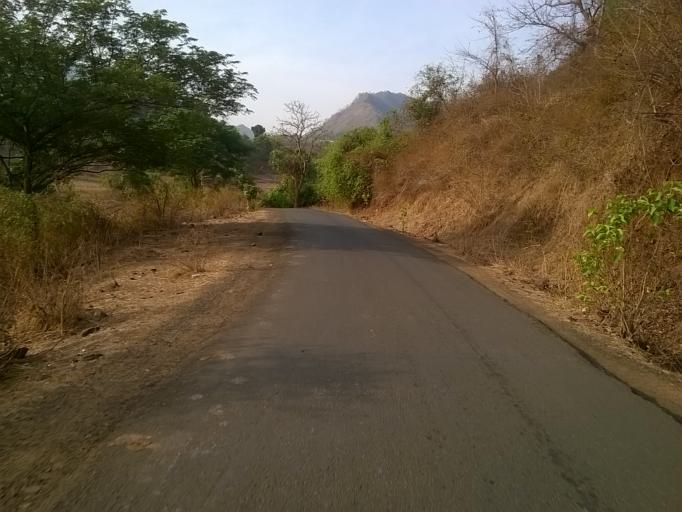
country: IN
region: Maharashtra
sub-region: Raigarh
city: Matheran
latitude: 19.0268
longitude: 73.2428
